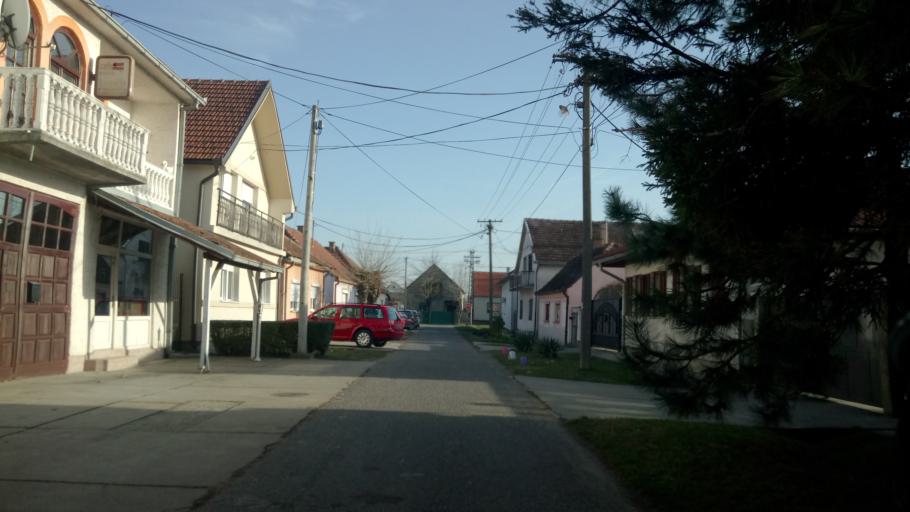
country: RS
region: Autonomna Pokrajina Vojvodina
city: Nova Pazova
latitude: 44.9475
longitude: 20.2316
